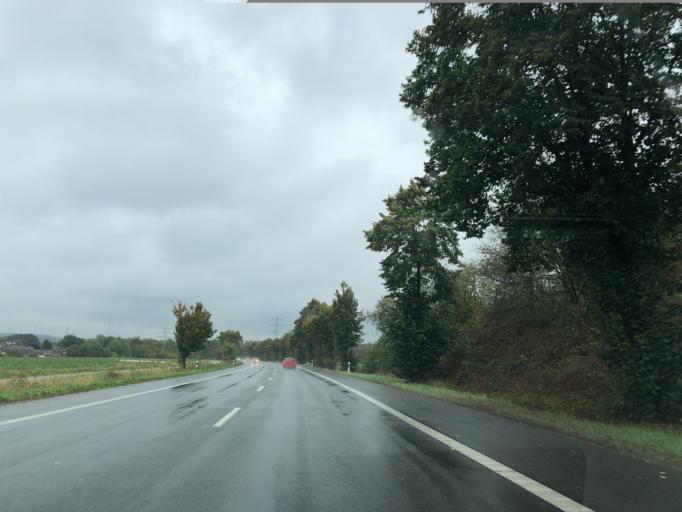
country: DE
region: North Rhine-Westphalia
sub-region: Regierungsbezirk Dusseldorf
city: Grevenbroich
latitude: 51.0674
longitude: 6.5571
